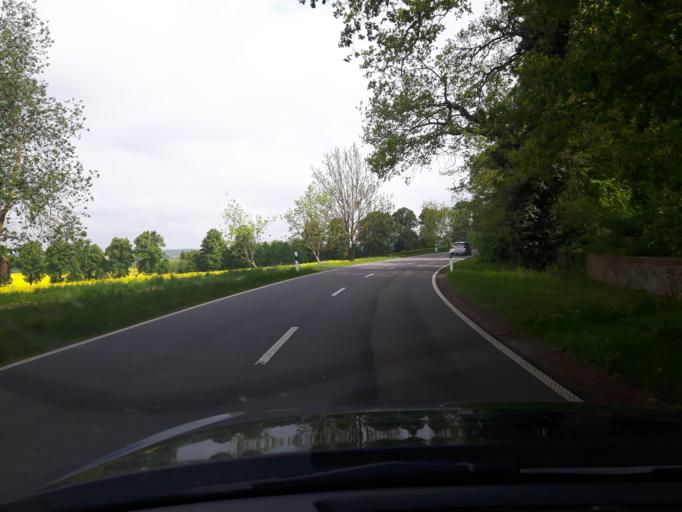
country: DE
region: Mecklenburg-Vorpommern
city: Gross Wokern
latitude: 53.6410
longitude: 12.4853
